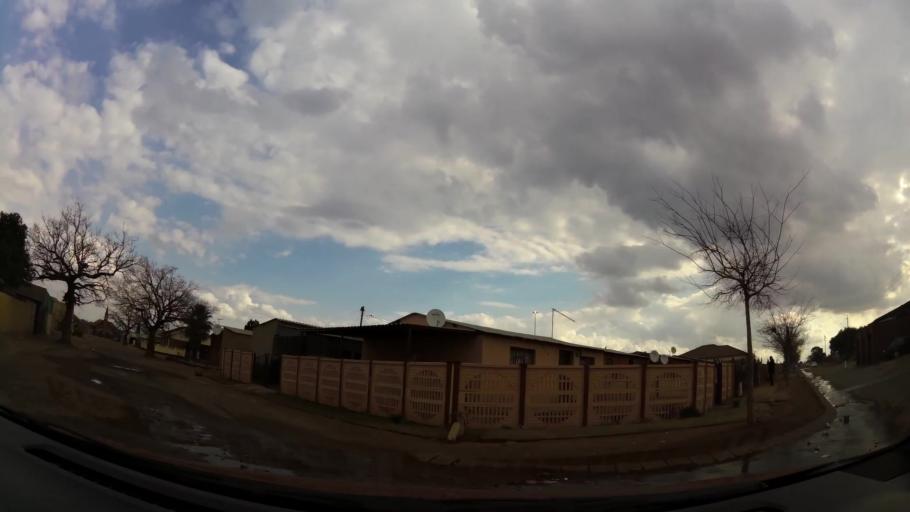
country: ZA
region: Gauteng
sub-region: Sedibeng District Municipality
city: Vanderbijlpark
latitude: -26.6637
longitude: 27.8536
